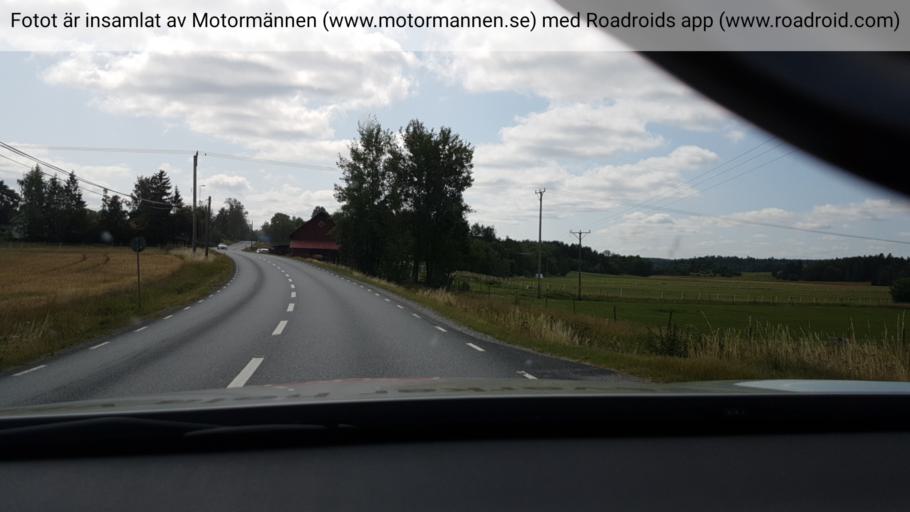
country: SE
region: Stockholm
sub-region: Vallentuna Kommun
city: Vallentuna
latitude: 59.5408
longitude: 18.1705
